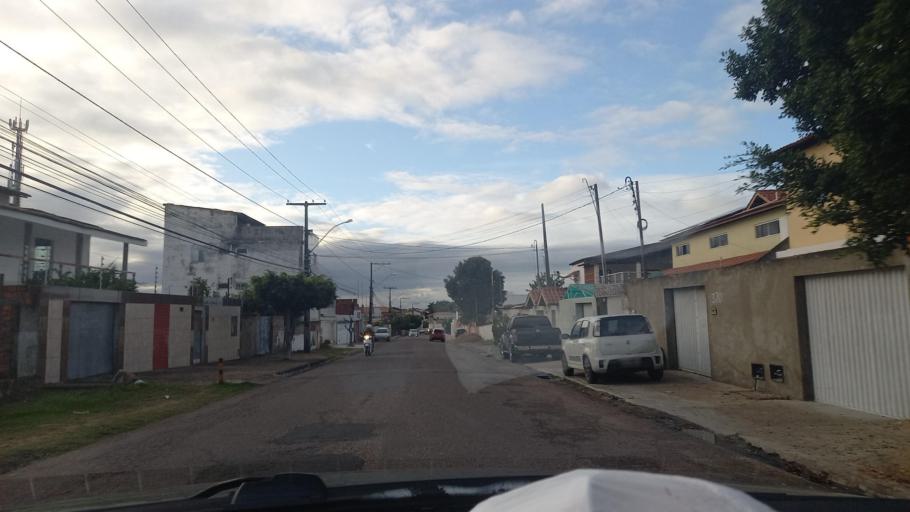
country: BR
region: Bahia
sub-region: Paulo Afonso
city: Paulo Afonso
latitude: -9.3979
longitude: -38.2373
